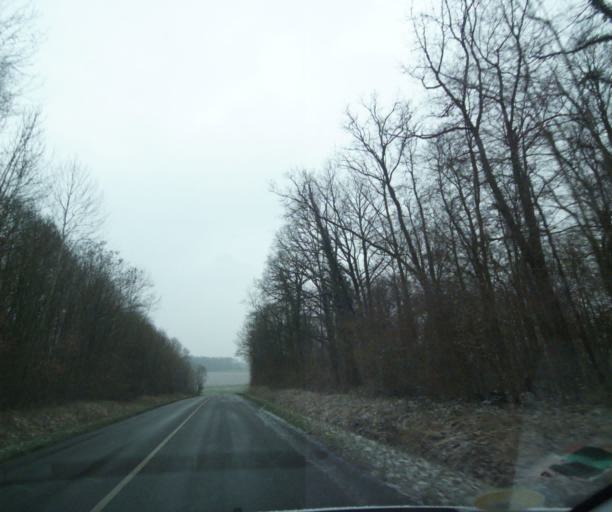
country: FR
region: Champagne-Ardenne
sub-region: Departement de la Haute-Marne
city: Wassy
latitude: 48.4717
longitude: 5.0217
